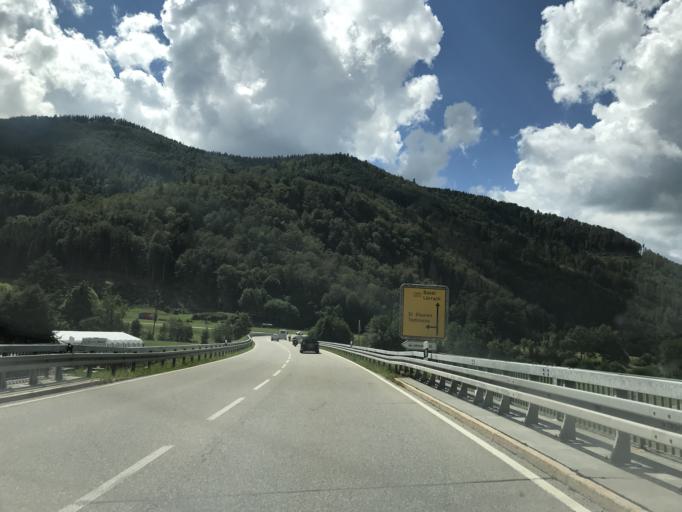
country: DE
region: Baden-Wuerttemberg
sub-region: Freiburg Region
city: Utzenfeld
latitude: 47.8064
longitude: 7.9349
